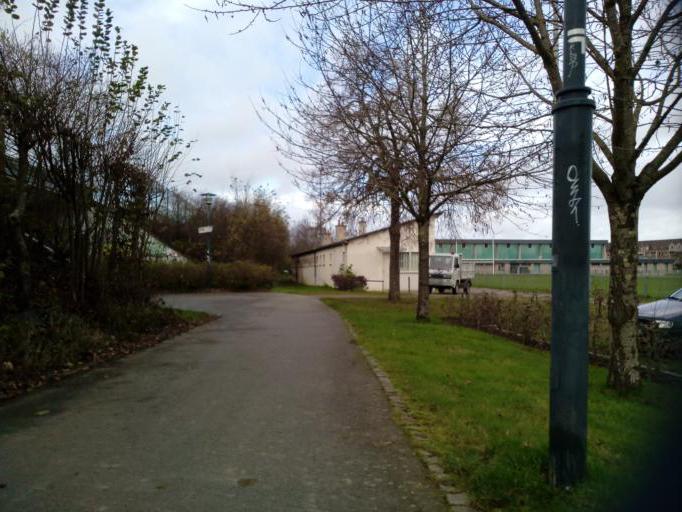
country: FR
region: Brittany
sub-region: Departement d'Ille-et-Vilaine
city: Chantepie
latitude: 48.0856
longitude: -1.6417
